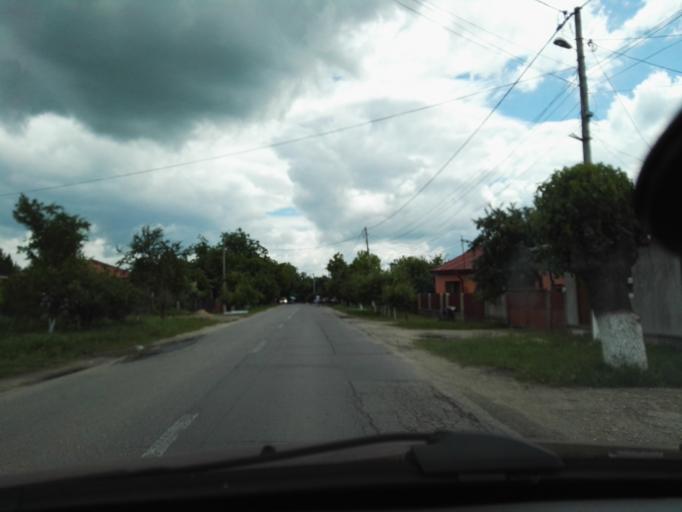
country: RO
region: Ilfov
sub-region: Comuna Copaceni
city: Copaceni
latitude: 44.2459
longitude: 26.0831
